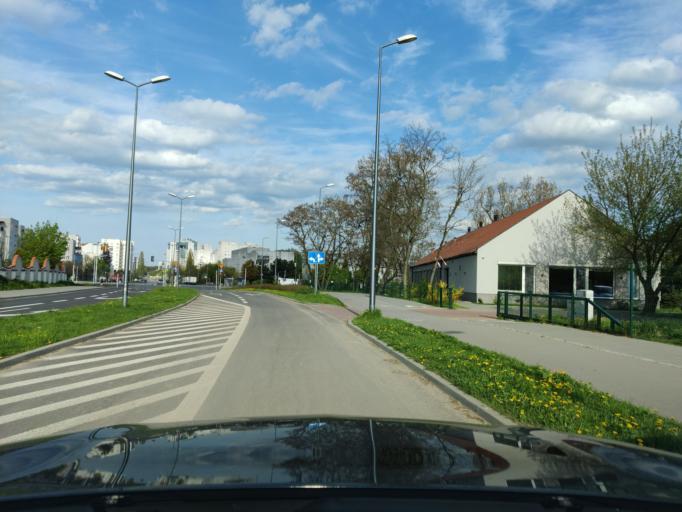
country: PL
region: Masovian Voivodeship
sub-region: Warszawa
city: Ursynow
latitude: 52.1370
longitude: 21.0477
